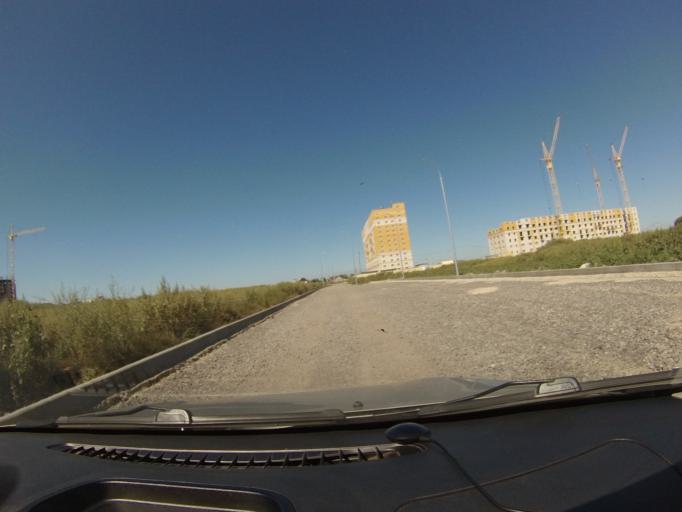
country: RU
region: Tambov
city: Tambov
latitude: 52.7771
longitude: 41.4077
